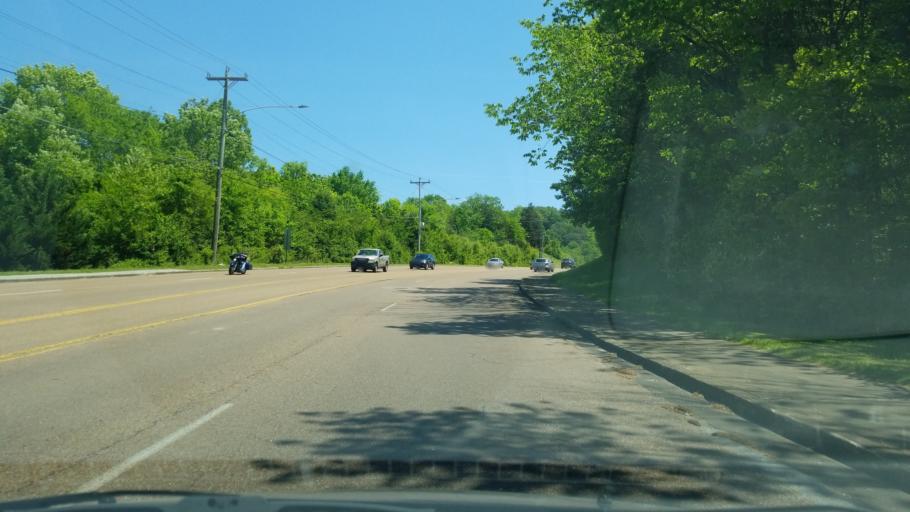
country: US
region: Tennessee
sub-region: Hamilton County
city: Red Bank
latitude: 35.1248
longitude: -85.3047
